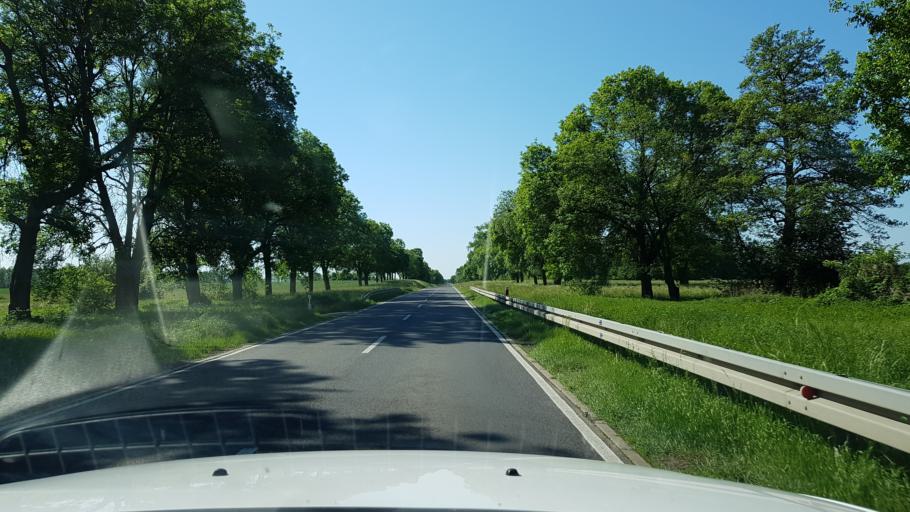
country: PL
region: West Pomeranian Voivodeship
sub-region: Powiat gryfinski
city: Mieszkowice
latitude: 52.8209
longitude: 14.4963
